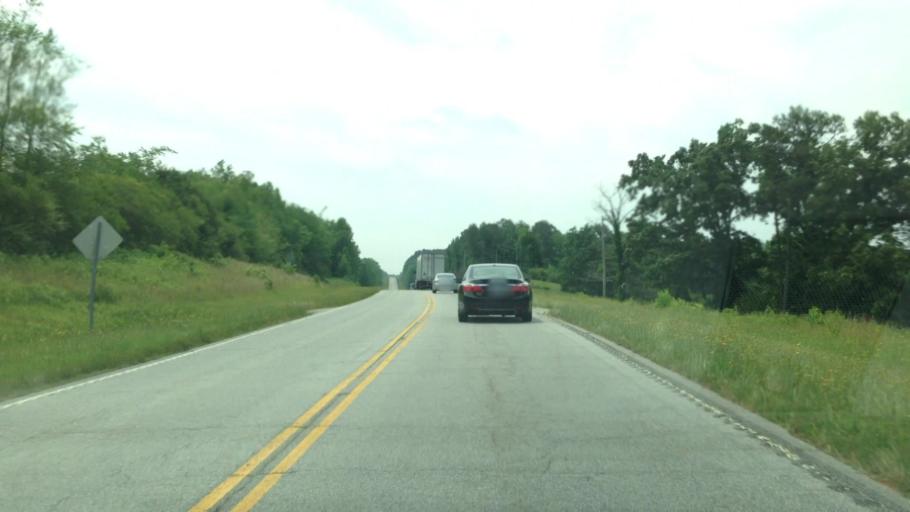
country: US
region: South Carolina
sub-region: Oconee County
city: Westminster
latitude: 34.6477
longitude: -83.0494
